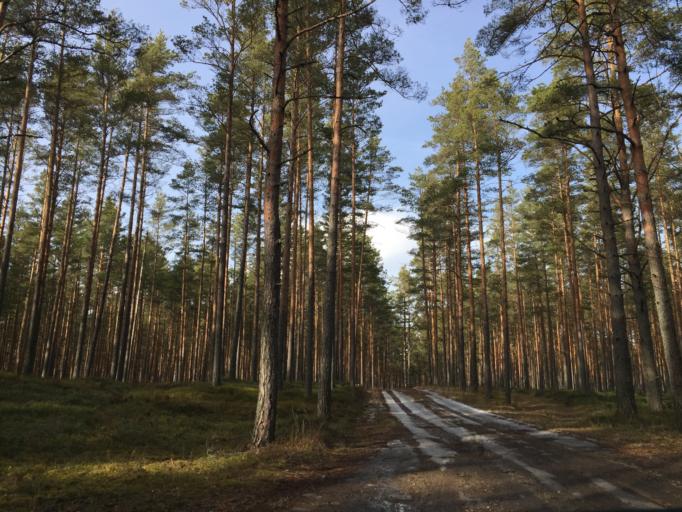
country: EE
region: Paernumaa
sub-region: Paernu linn
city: Parnu
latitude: 58.2340
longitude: 24.5184
